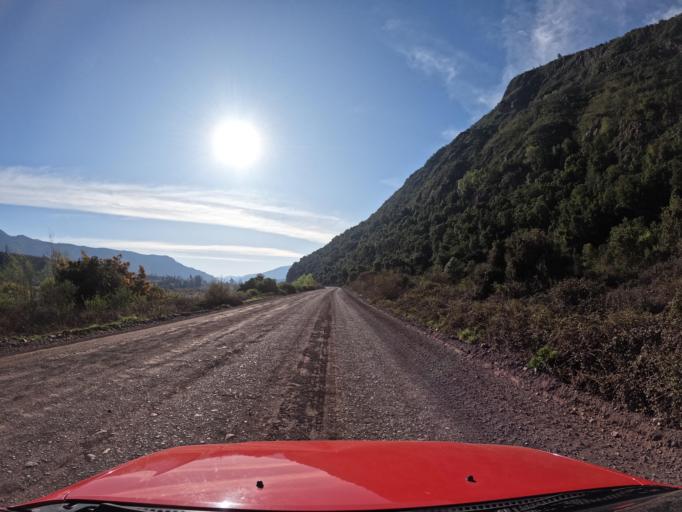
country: CL
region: Maule
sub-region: Provincia de Curico
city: Teno
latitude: -34.9998
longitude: -70.8421
